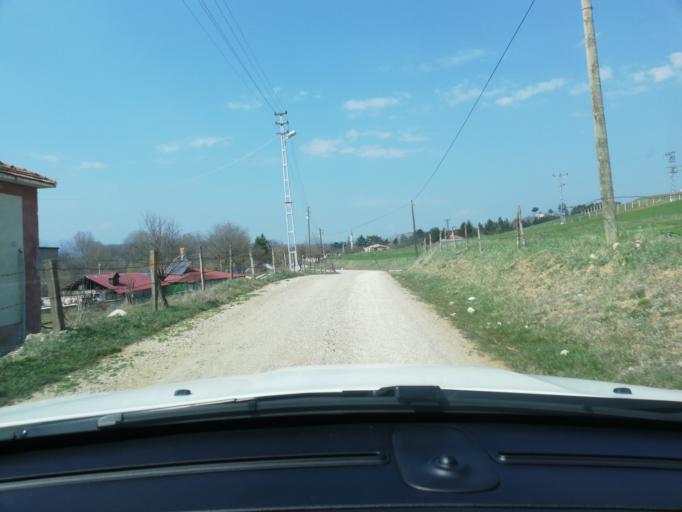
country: TR
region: Kastamonu
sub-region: Cide
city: Kastamonu
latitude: 41.4612
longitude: 33.7503
